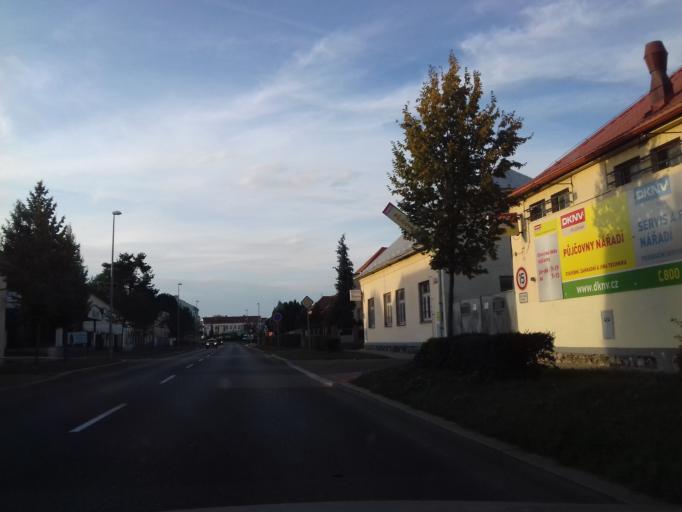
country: CZ
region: Praha
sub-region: Praha 4
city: Hodkovicky
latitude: 50.0122
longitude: 14.4586
